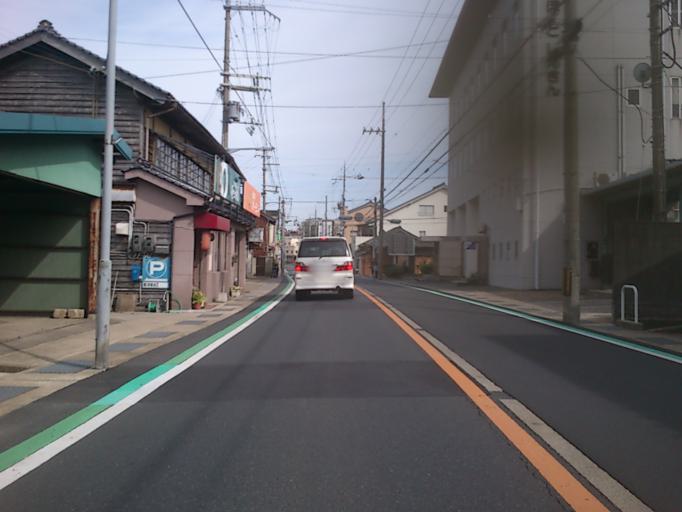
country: JP
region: Kyoto
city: Miyazu
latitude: 35.6826
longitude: 135.0264
